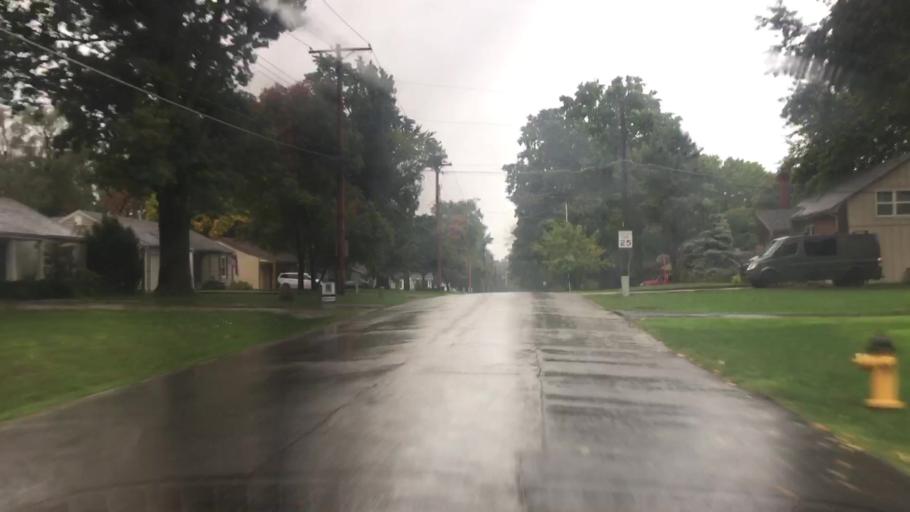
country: US
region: Kansas
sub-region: Johnson County
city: Shawnee
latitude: 39.0333
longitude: -94.7286
